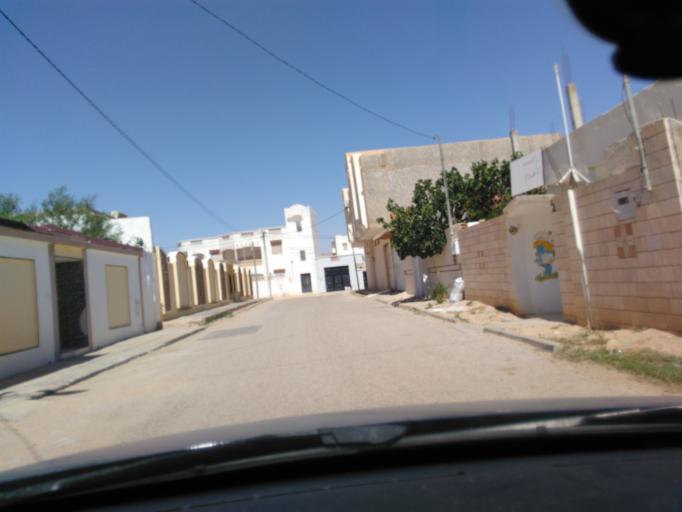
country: TN
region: Tataouine
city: Tataouine
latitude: 32.9506
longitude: 10.4694
